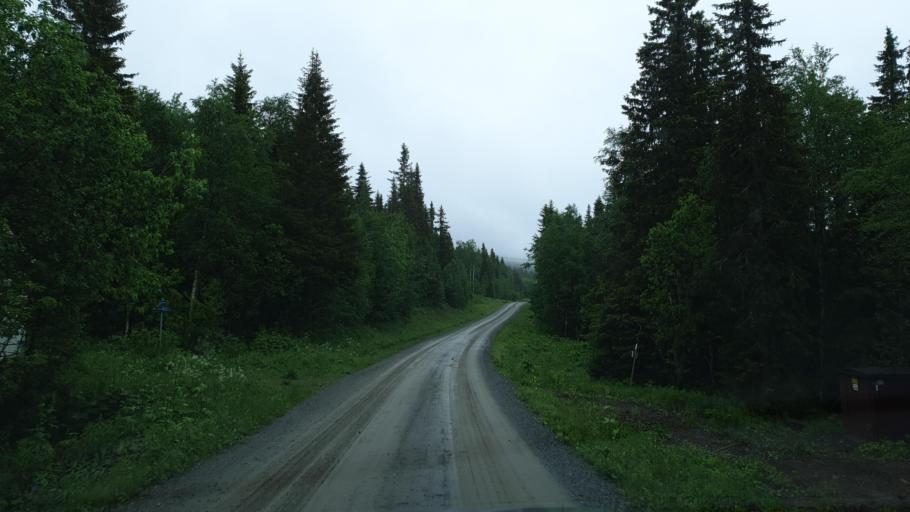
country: SE
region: Vaesterbotten
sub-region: Vilhelmina Kommun
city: Sjoberg
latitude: 65.3449
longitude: 15.8727
